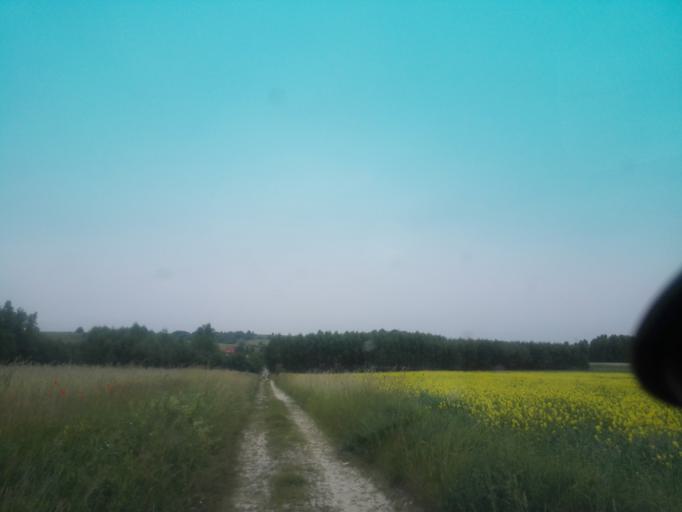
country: PL
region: Silesian Voivodeship
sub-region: Powiat czestochowski
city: Mstow
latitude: 50.7919
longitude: 19.3620
